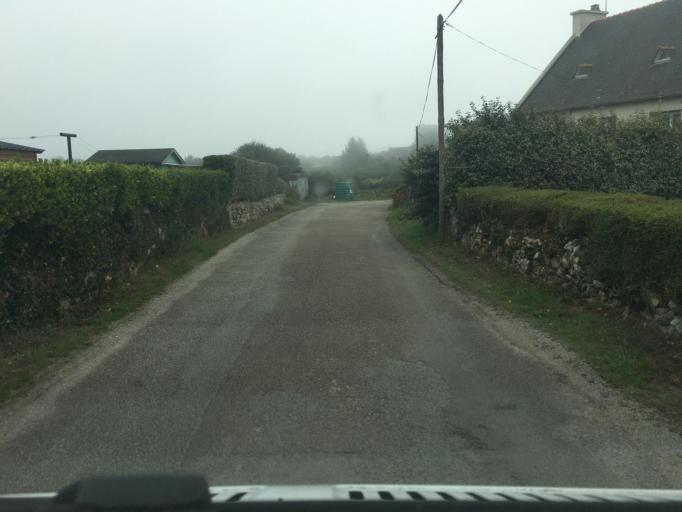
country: FR
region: Brittany
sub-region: Departement du Finistere
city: Plogoff
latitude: 48.0392
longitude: -4.6914
